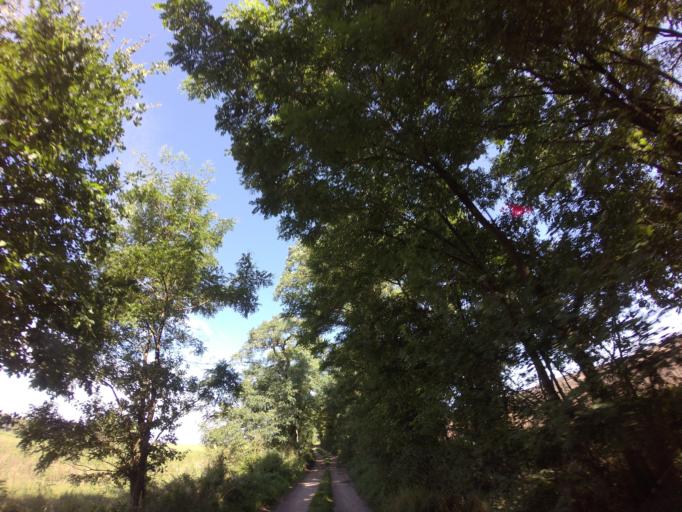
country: PL
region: West Pomeranian Voivodeship
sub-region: Powiat choszczenski
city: Recz
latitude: 53.2011
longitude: 15.5011
